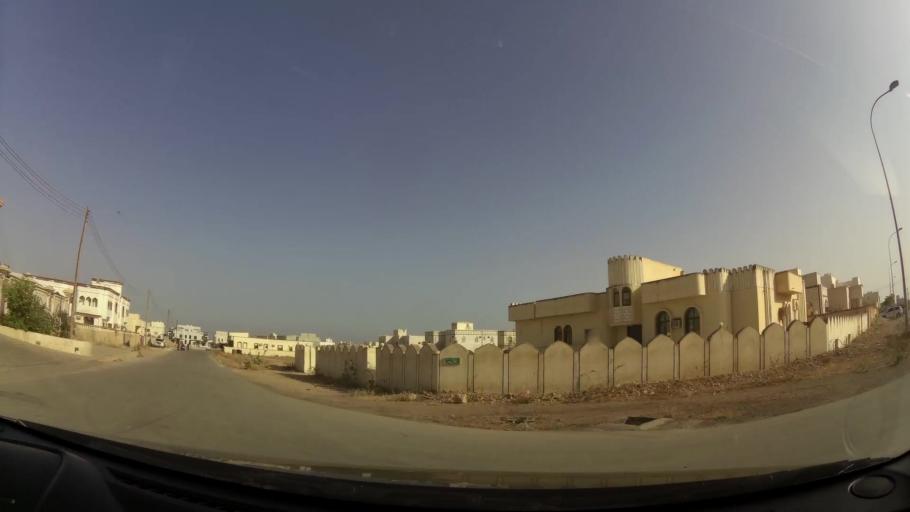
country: OM
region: Zufar
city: Salalah
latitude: 17.0233
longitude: 54.0201
